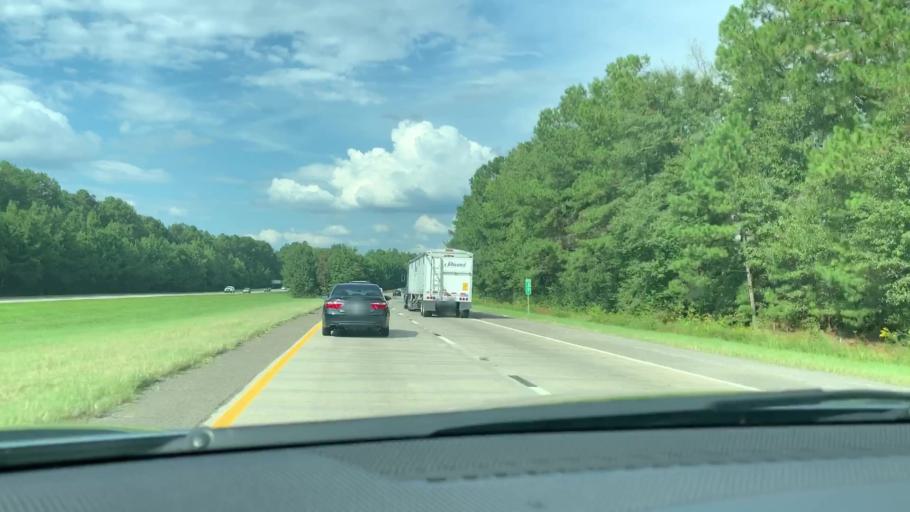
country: US
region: South Carolina
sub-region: Hampton County
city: Yemassee
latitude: 32.6879
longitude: -80.8807
